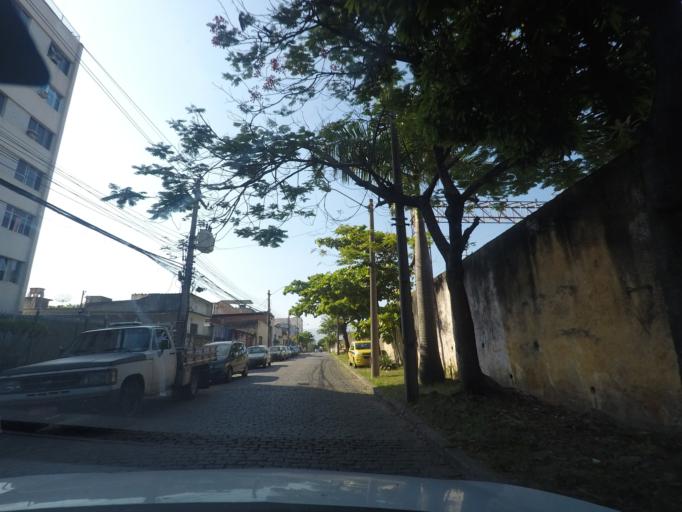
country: BR
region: Rio de Janeiro
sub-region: Rio De Janeiro
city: Rio de Janeiro
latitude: -22.8613
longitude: -43.2572
